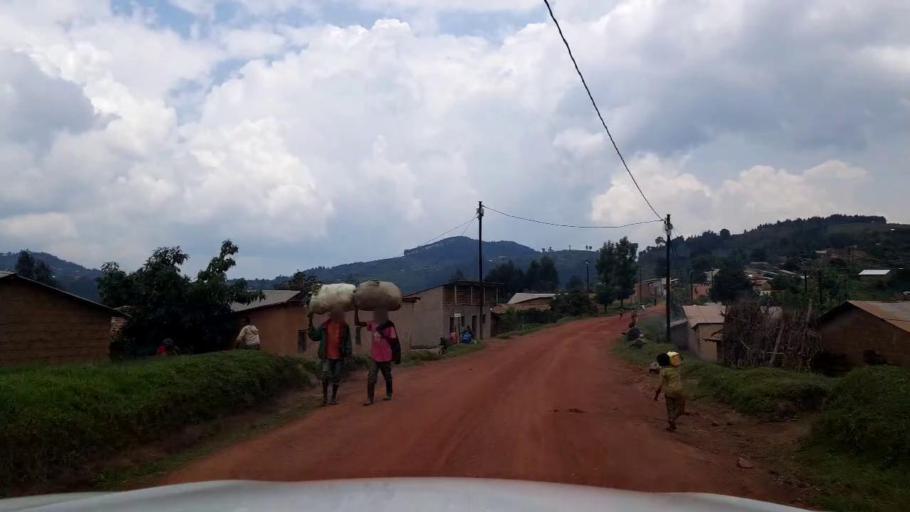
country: RW
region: Northern Province
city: Byumba
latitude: -1.5177
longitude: 29.9450
